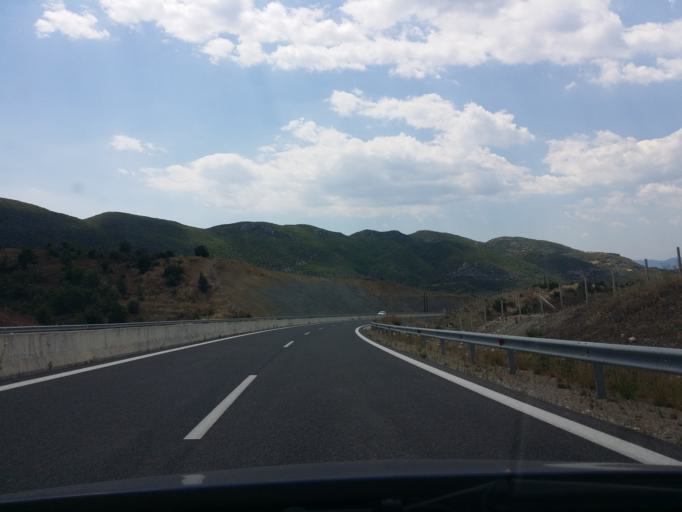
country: GR
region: Peloponnese
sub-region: Nomos Arkadias
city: Megalopoli
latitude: 37.3099
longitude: 22.1744
